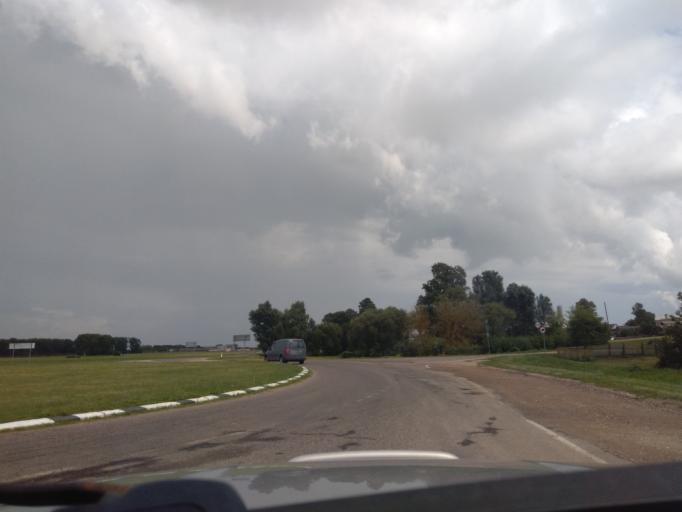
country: BY
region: Minsk
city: Tsimkavichy
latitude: 53.0740
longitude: 26.9857
